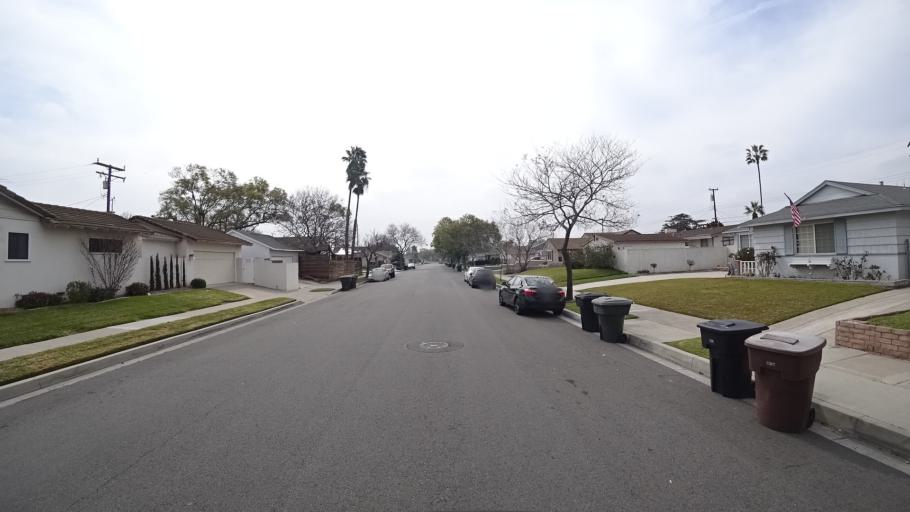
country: US
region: California
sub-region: Orange County
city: Anaheim
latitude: 33.8236
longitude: -117.9459
